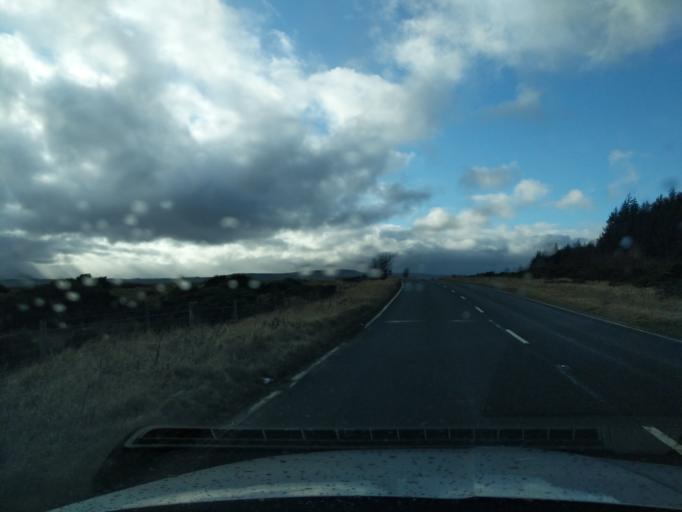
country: GB
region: England
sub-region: North Yorkshire
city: Leyburn
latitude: 54.3484
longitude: -1.7857
